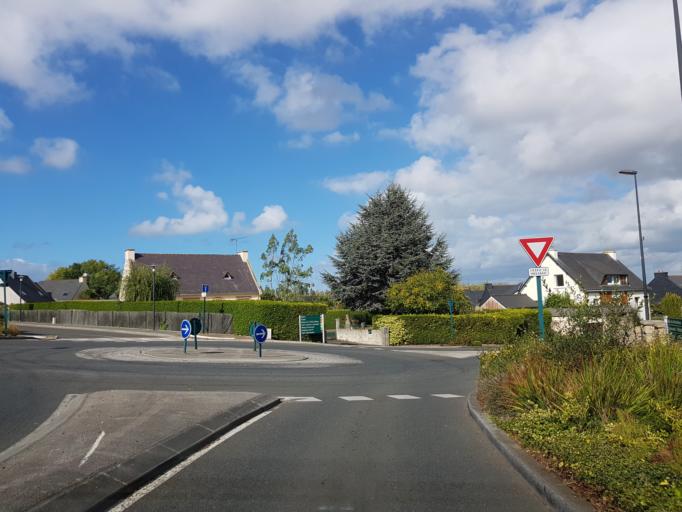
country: FR
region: Brittany
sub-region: Departement des Cotes-d'Armor
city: Yffiniac
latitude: 48.4825
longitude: -2.6813
